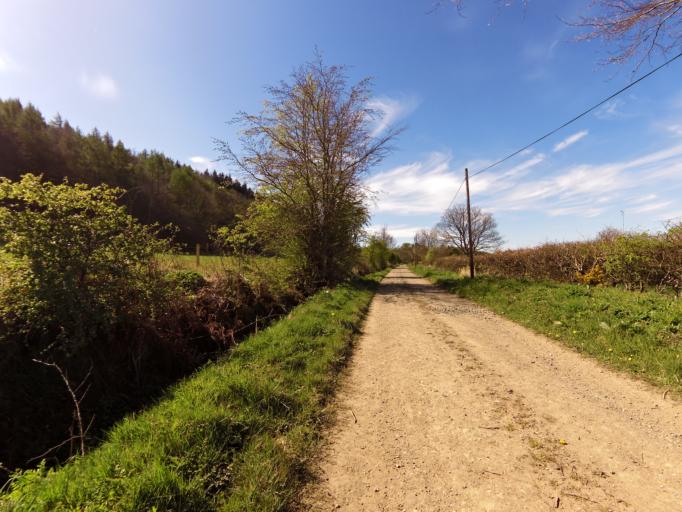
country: GB
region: Scotland
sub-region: Fife
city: Cupar
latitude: 56.3972
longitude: -3.0665
